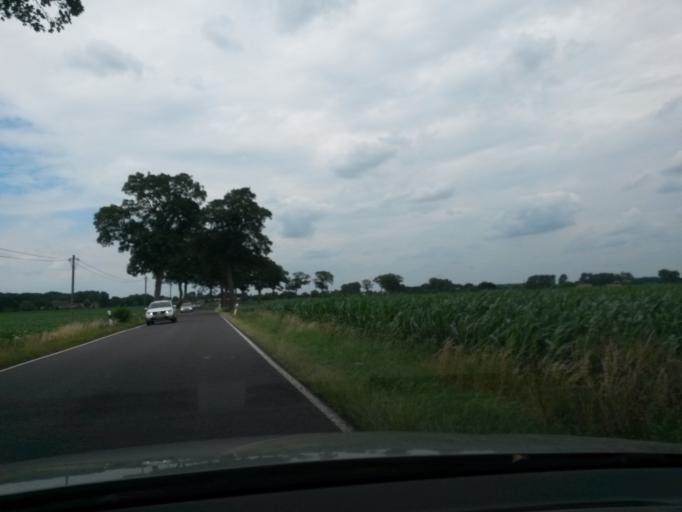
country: DE
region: North Rhine-Westphalia
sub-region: Regierungsbezirk Dusseldorf
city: Viersen
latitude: 51.2965
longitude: 6.3880
